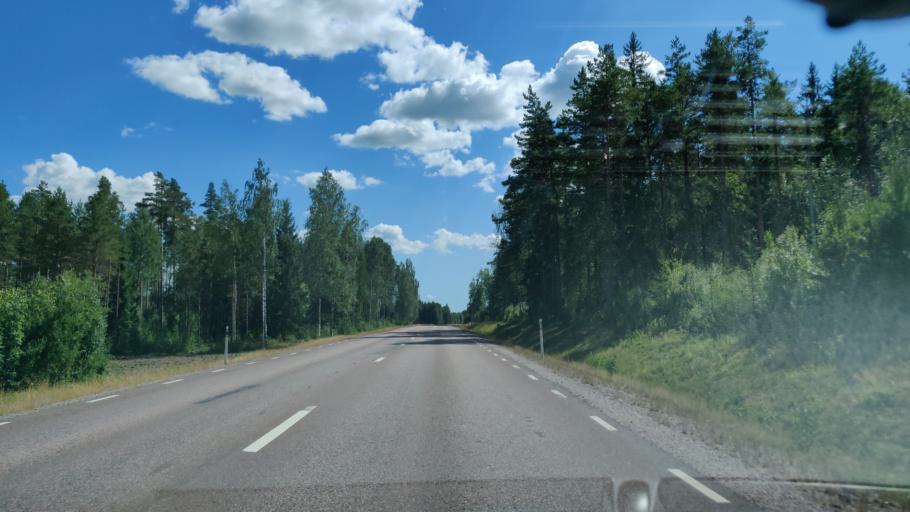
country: SE
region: Vaermland
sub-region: Hagfors Kommun
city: Ekshaerad
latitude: 60.2086
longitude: 13.4877
